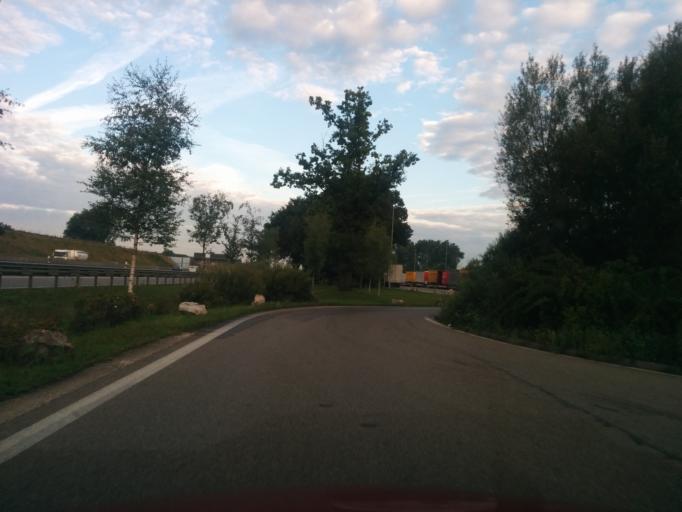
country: DE
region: Bavaria
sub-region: Swabia
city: Augsburg
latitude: 48.4113
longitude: 10.9136
